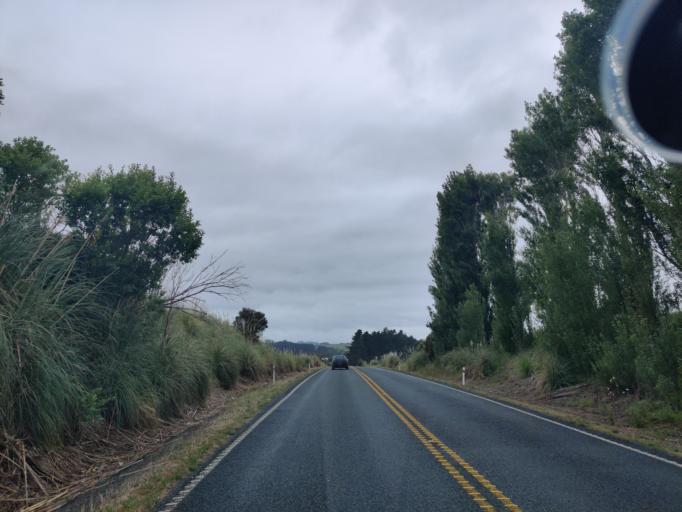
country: NZ
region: Northland
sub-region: Kaipara District
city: Dargaville
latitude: -36.1265
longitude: 174.1634
